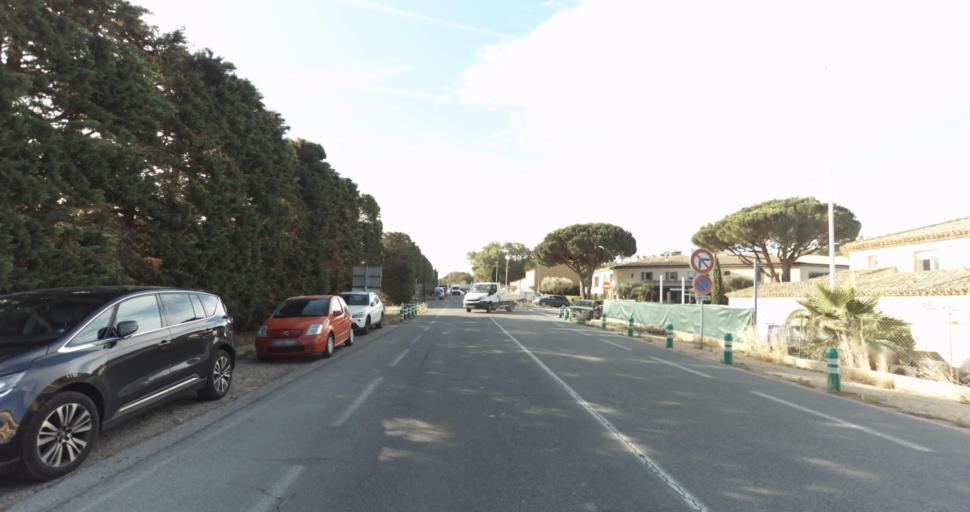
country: FR
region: Provence-Alpes-Cote d'Azur
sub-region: Departement du Var
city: Saint-Tropez
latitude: 43.2582
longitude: 6.6332
